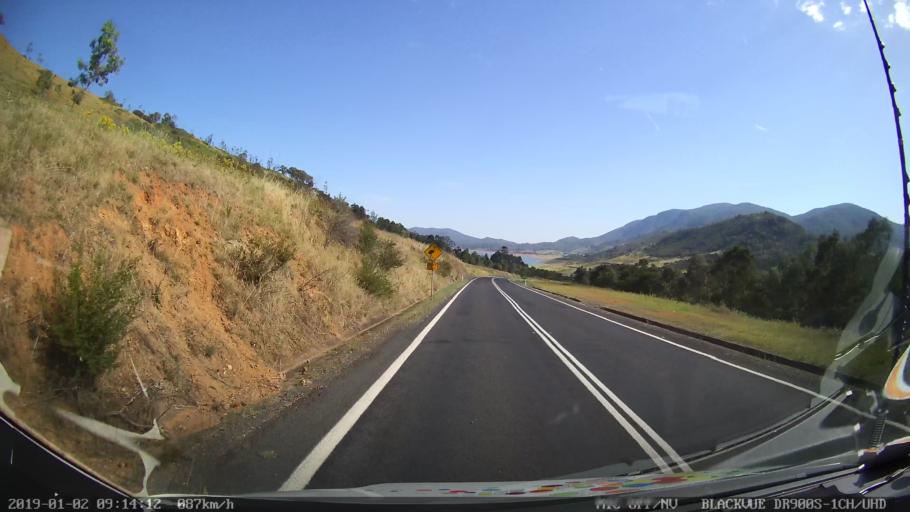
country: AU
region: New South Wales
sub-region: Tumut Shire
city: Tumut
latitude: -35.4803
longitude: 148.2727
